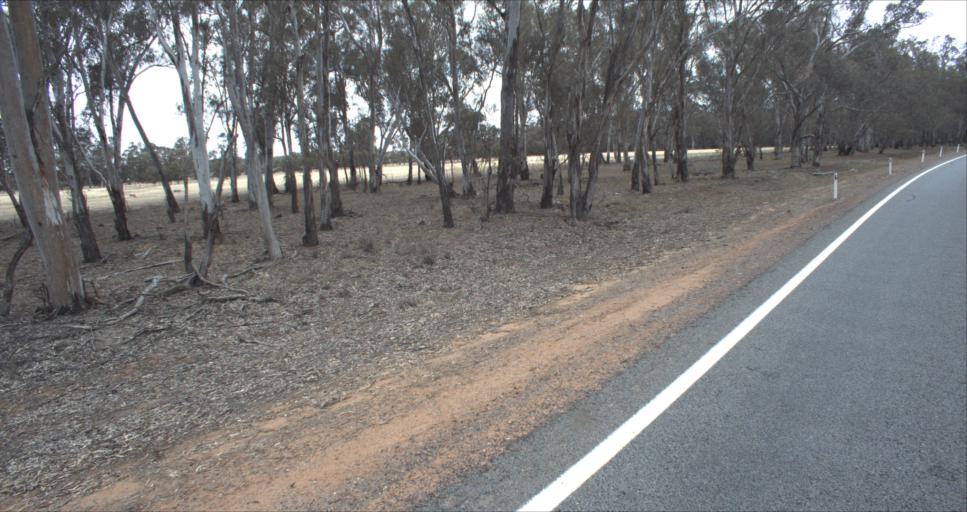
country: AU
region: New South Wales
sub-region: Leeton
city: Leeton
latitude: -34.6296
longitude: 146.3766
